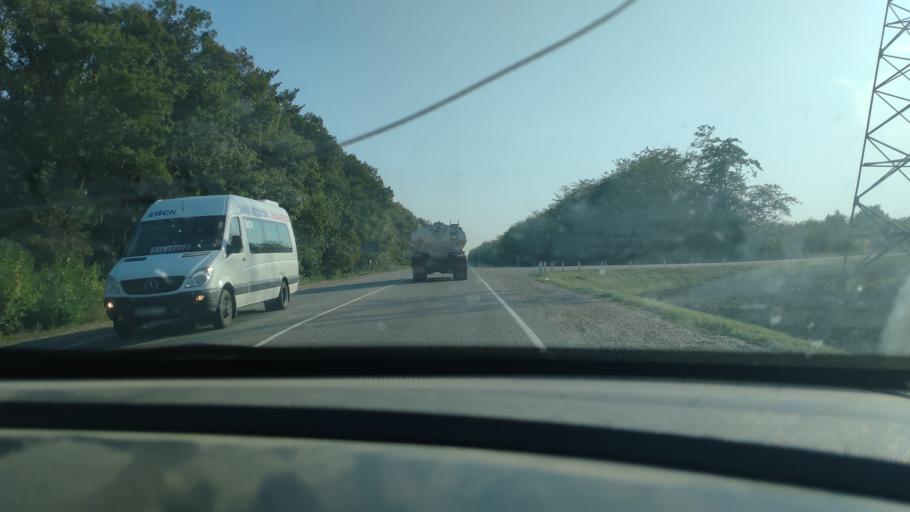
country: RU
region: Krasnodarskiy
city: Starominskaya
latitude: 46.4901
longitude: 39.0581
